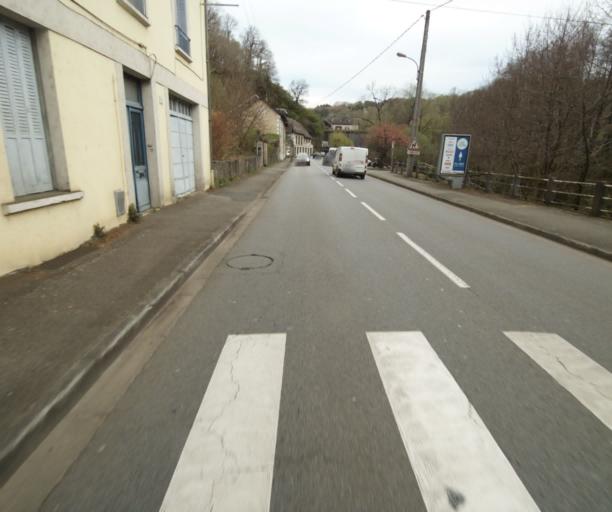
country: FR
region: Limousin
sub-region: Departement de la Correze
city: Tulle
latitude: 45.2544
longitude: 1.7636
